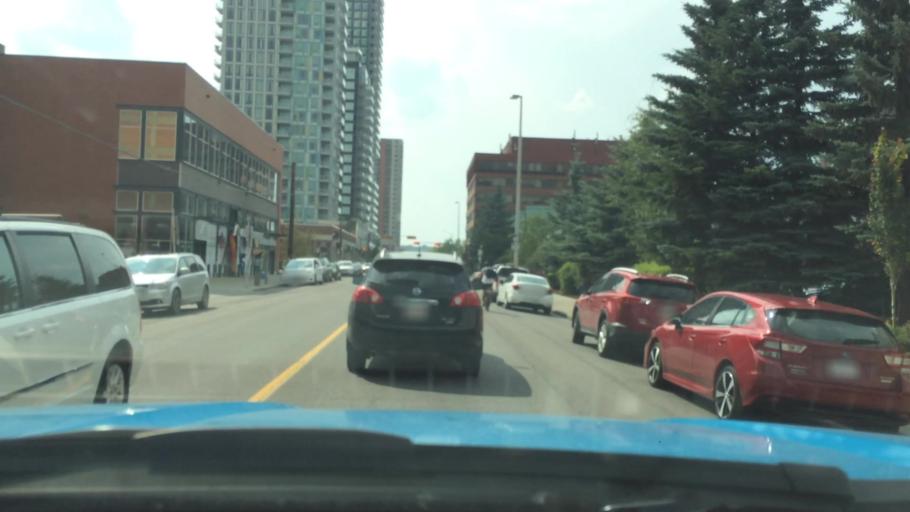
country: CA
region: Alberta
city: Calgary
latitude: 51.0438
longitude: -114.0790
